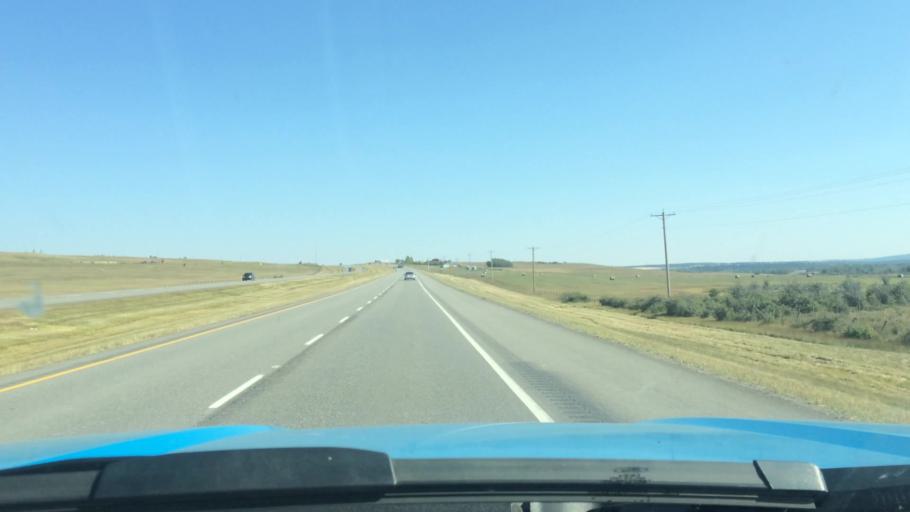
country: CA
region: Alberta
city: Cochrane
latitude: 51.0931
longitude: -114.5883
